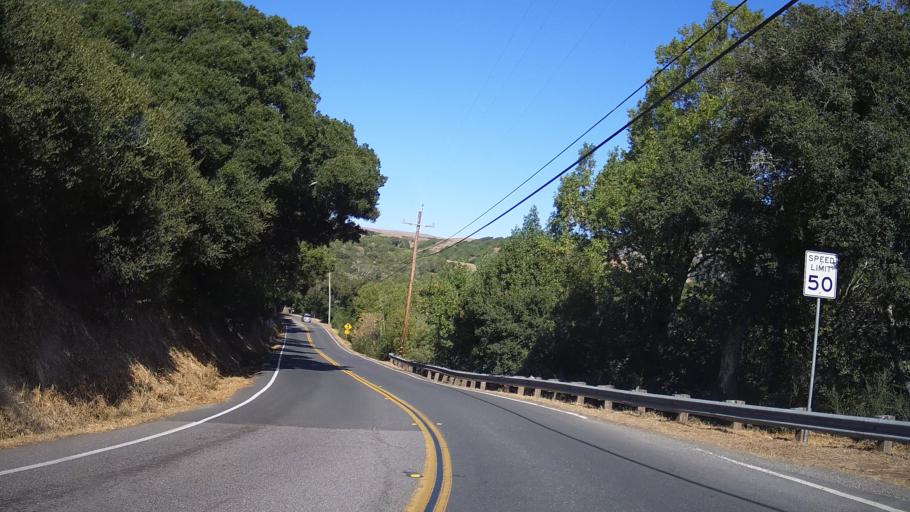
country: US
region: California
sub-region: Marin County
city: Inverness
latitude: 38.0731
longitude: -122.7999
